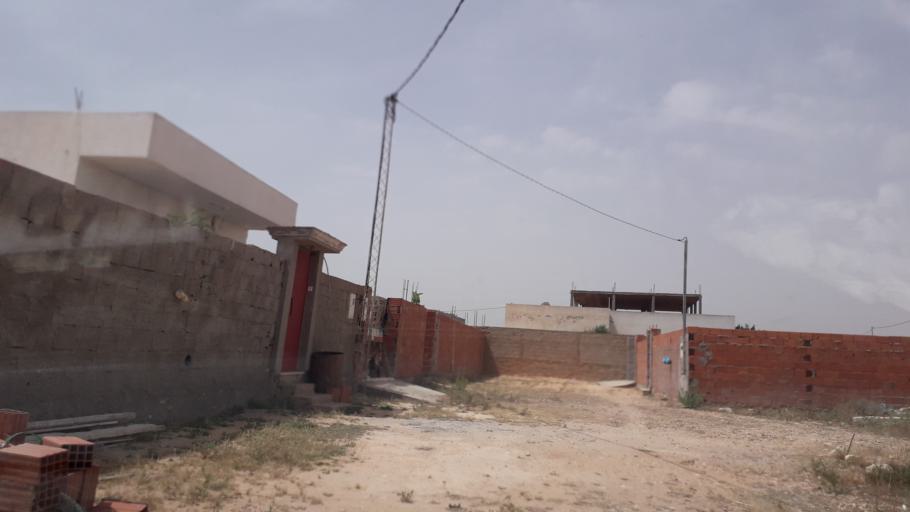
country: TN
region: Safaqis
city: Al Qarmadah
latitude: 34.8441
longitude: 10.7757
